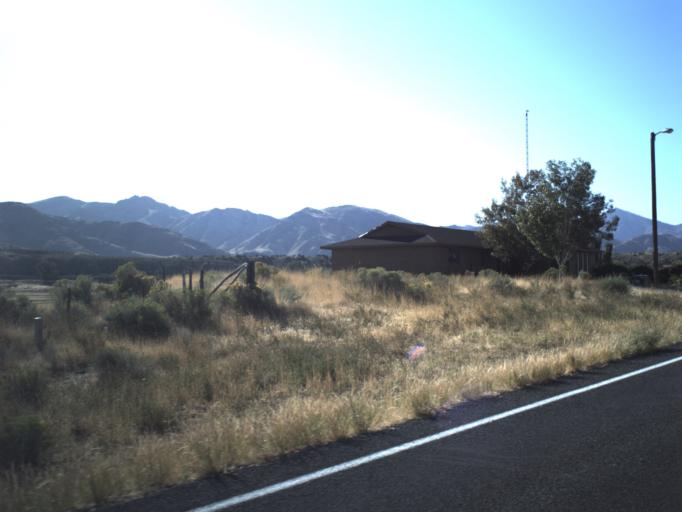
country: US
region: Utah
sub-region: Millard County
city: Delta
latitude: 39.5269
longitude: -112.2734
